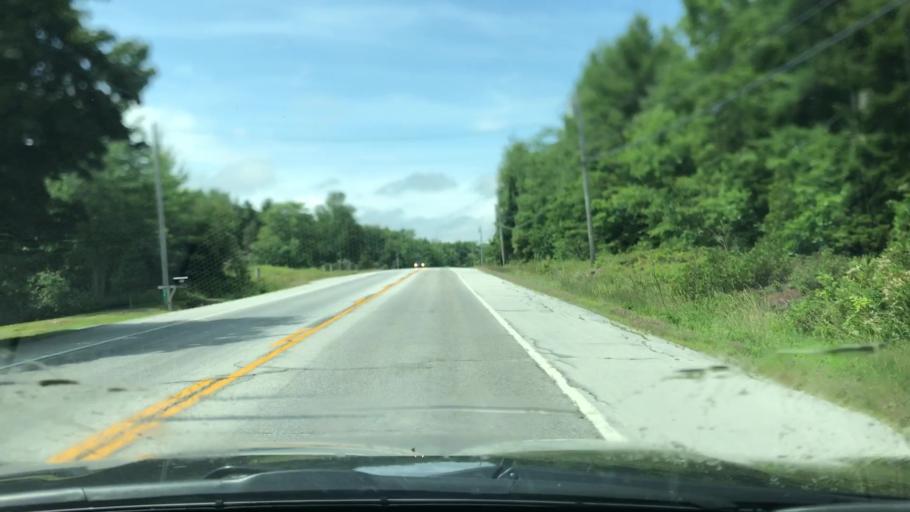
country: US
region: Maine
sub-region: Waldo County
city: Northport
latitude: 44.3581
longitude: -68.9715
